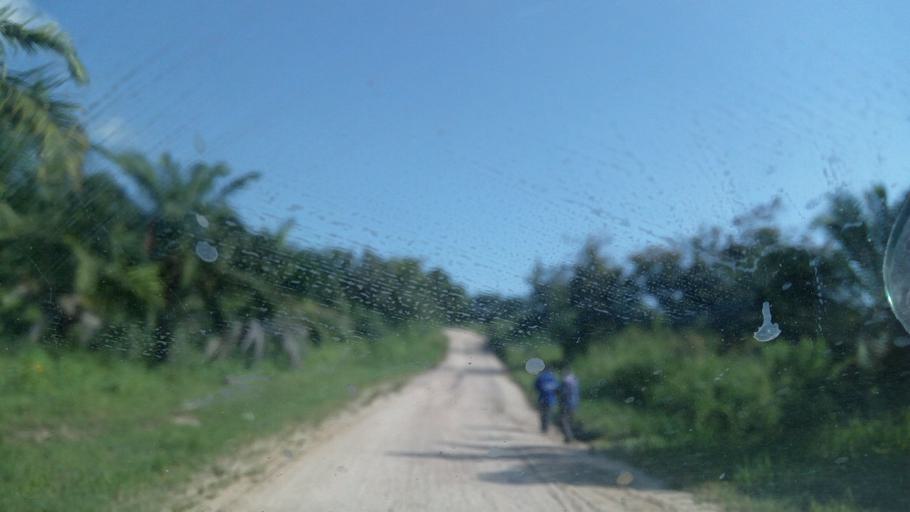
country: BI
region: Bururi
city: Rumonge
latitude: -3.9294
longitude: 29.1017
